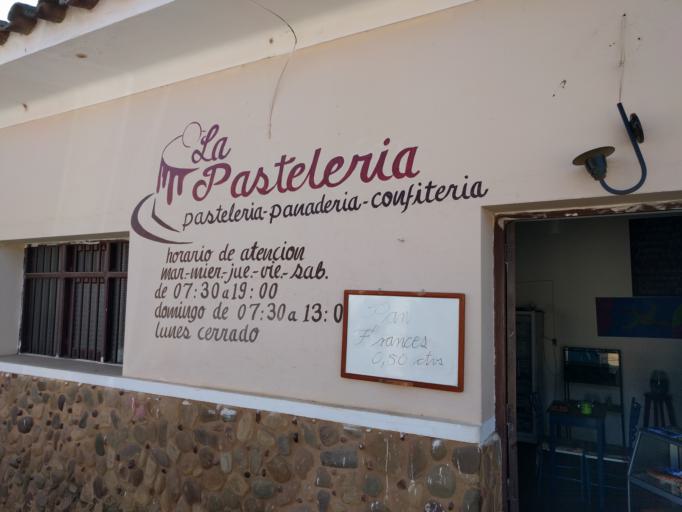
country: BO
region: Santa Cruz
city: Samaipata
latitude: -18.1786
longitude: -63.8747
